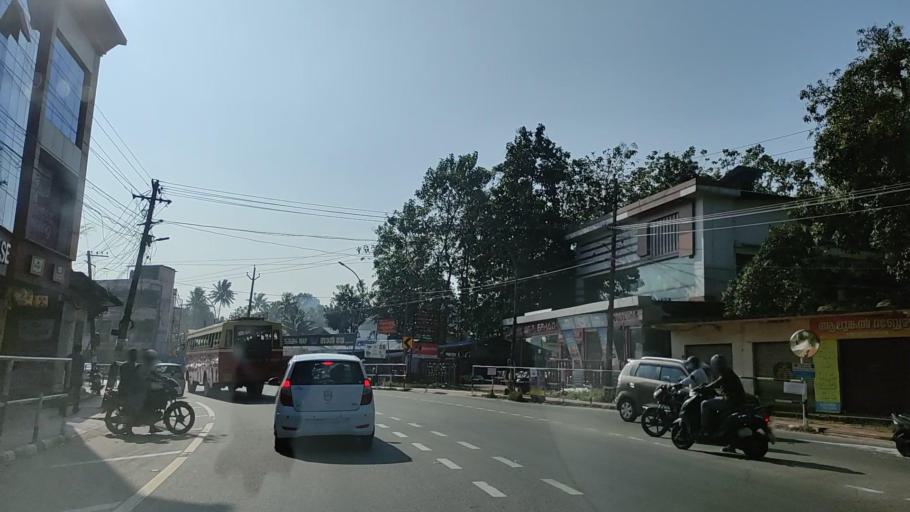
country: IN
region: Kerala
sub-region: Kollam
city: Punalur
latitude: 8.9001
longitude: 76.8575
